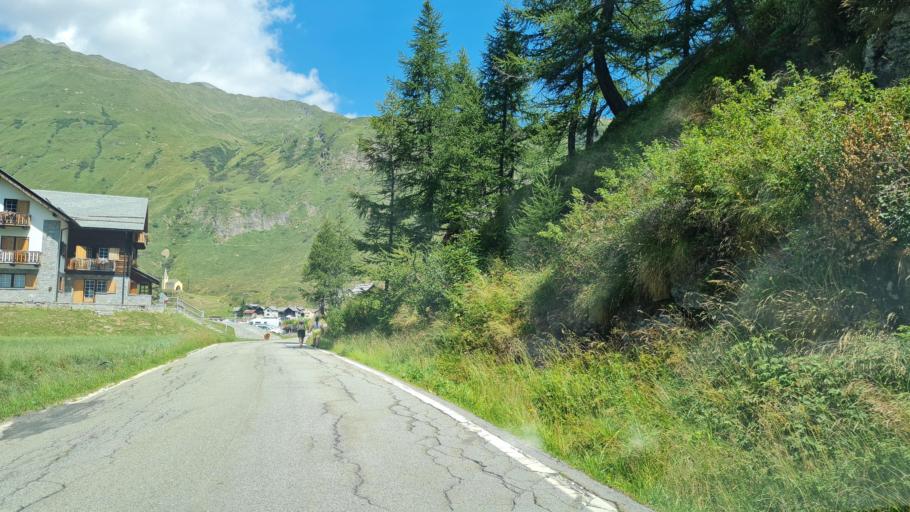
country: IT
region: Piedmont
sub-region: Provincia Verbano-Cusio-Ossola
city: Formazza
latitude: 46.4186
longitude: 8.4166
